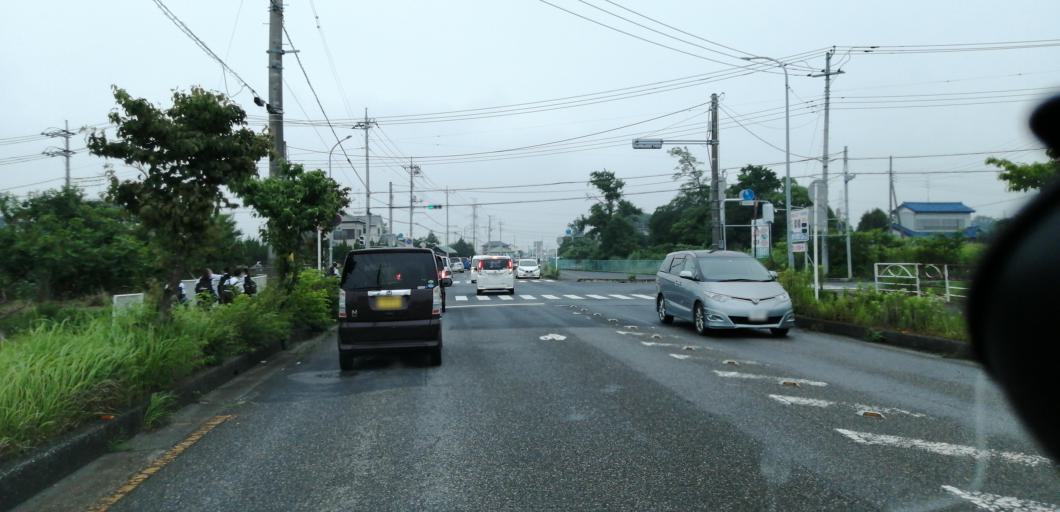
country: JP
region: Saitama
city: Kukichuo
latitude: 36.0987
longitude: 139.6841
